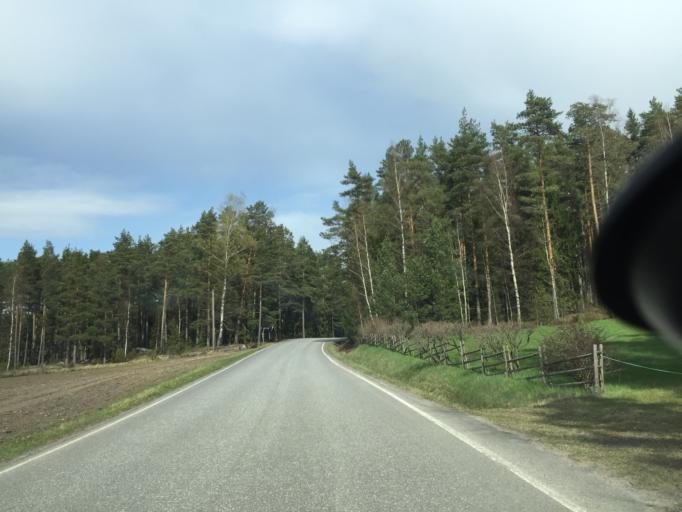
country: FI
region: Uusimaa
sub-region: Raaseporin
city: Hanko
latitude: 59.9710
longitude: 22.9860
